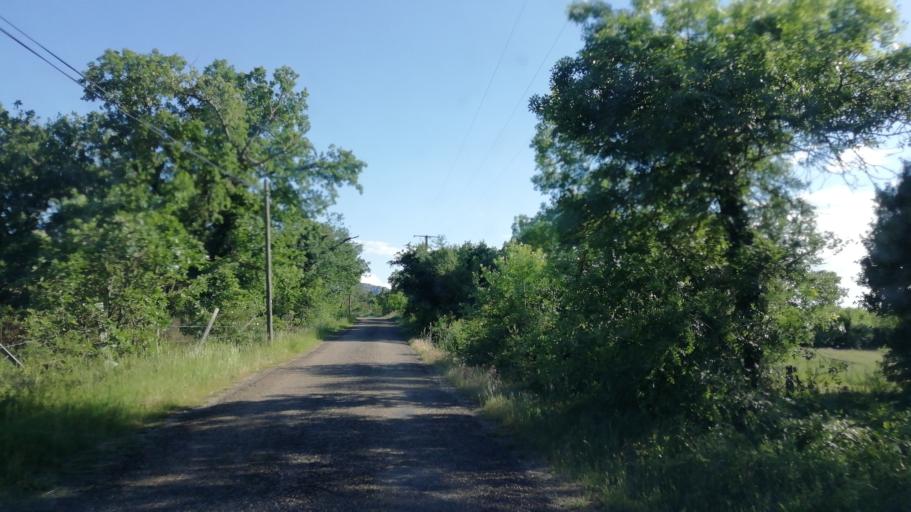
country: FR
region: Languedoc-Roussillon
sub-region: Departement de l'Herault
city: Saint-Mathieu-de-Treviers
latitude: 43.8145
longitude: 3.8135
